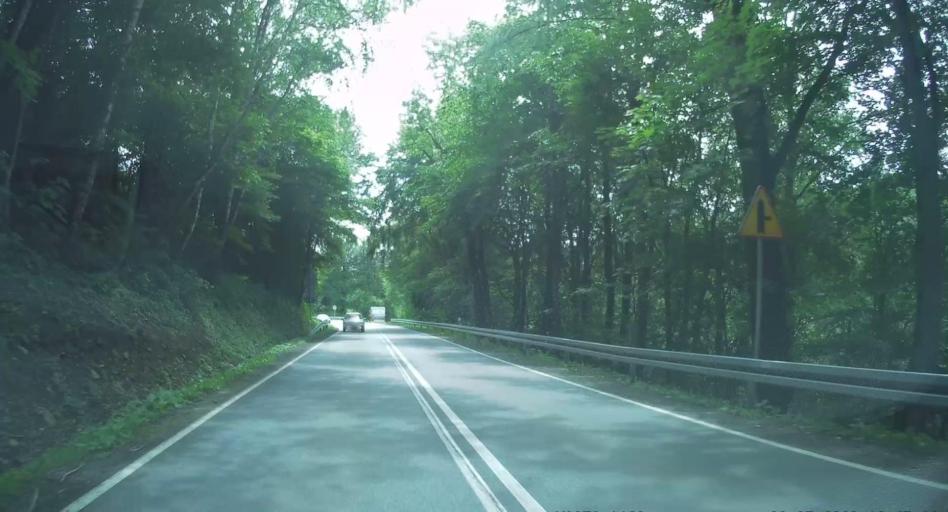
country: PL
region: Lesser Poland Voivodeship
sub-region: Powiat nowosadecki
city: Muszyna
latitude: 49.3486
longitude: 20.8020
